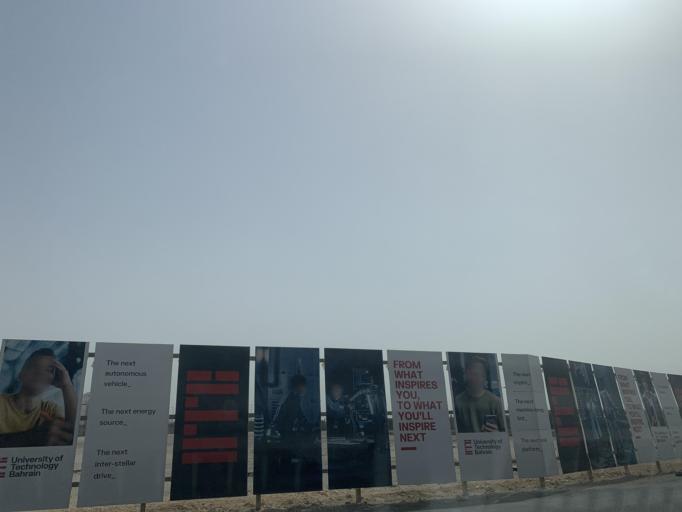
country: BH
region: Northern
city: Madinat `Isa
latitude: 26.1846
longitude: 50.5184
